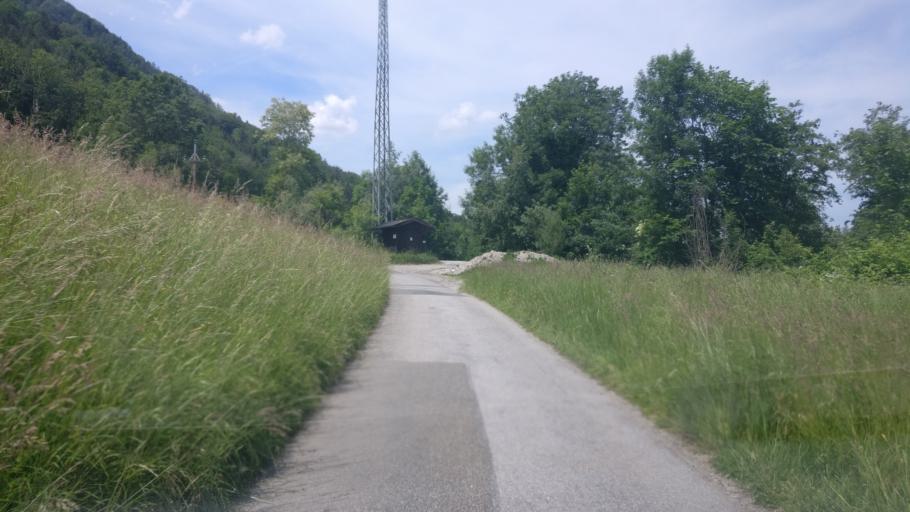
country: AT
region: Salzburg
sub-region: Politischer Bezirk Hallein
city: Adnet
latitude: 47.6555
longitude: 13.1185
